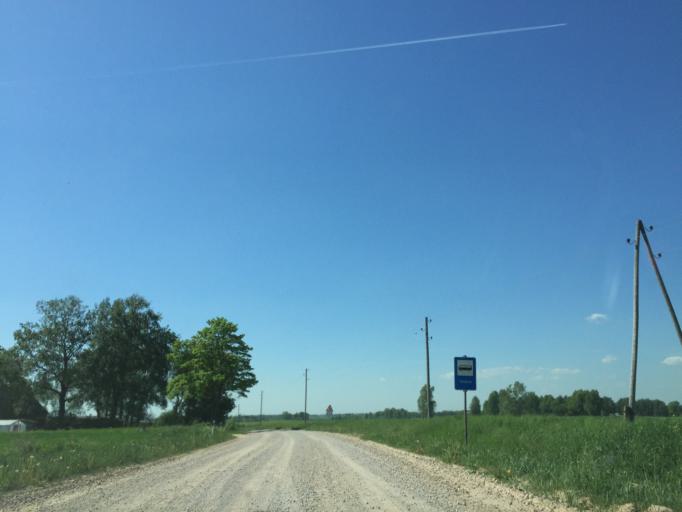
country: LV
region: Rundales
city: Pilsrundale
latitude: 56.4924
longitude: 24.0750
